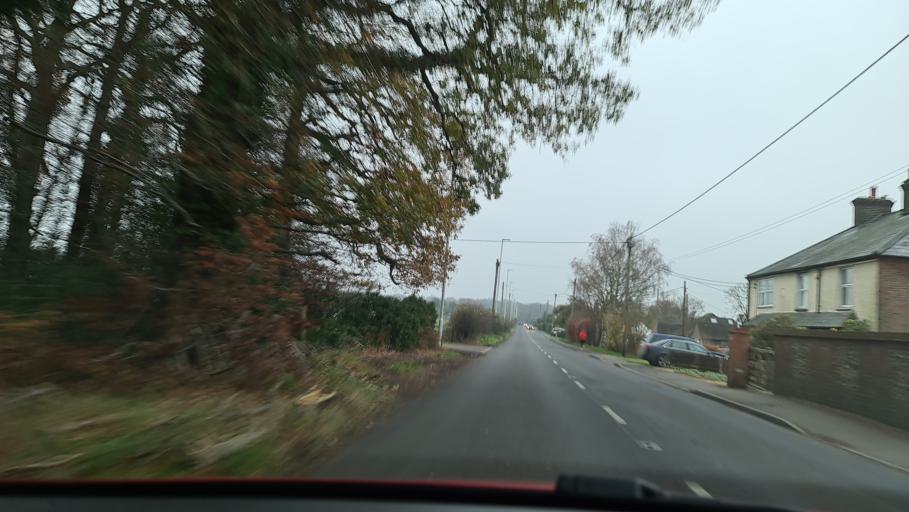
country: GB
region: England
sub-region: Buckinghamshire
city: High Wycombe
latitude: 51.6498
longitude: -0.7037
